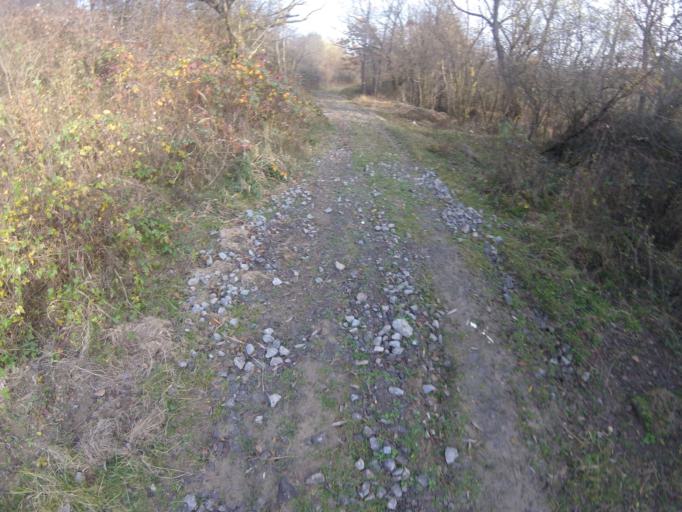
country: HU
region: Borsod-Abauj-Zemplen
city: Sarospatak
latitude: 48.4332
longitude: 21.5197
